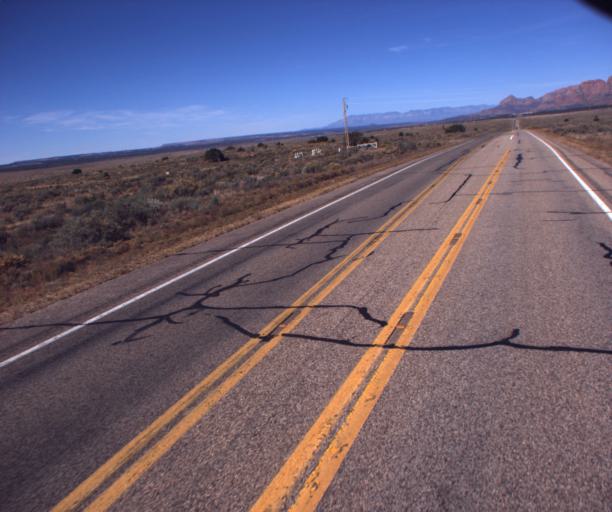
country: US
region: Arizona
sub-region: Mohave County
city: Colorado City
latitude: 36.9030
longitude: -112.9212
